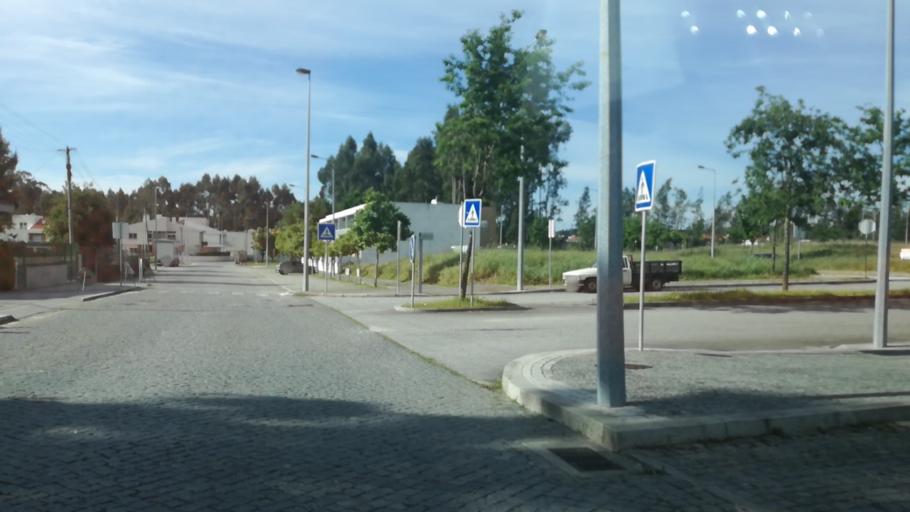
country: PT
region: Porto
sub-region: Maia
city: Nogueira
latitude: 41.2411
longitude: -8.5934
